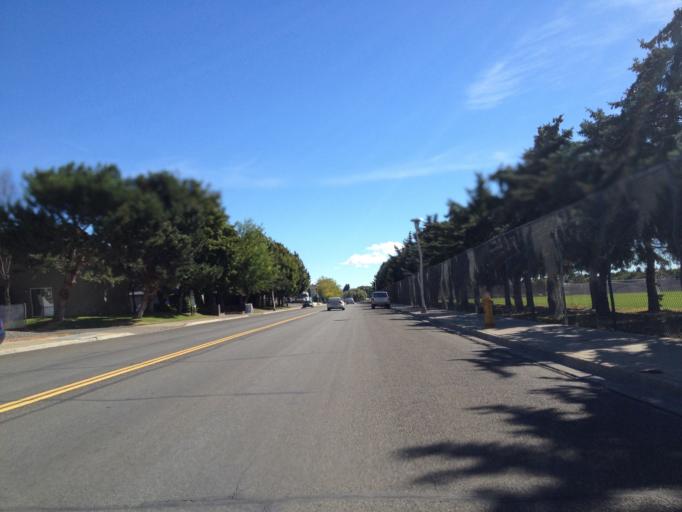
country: US
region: Washington
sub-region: Kittitas County
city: Ellensburg
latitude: 47.0103
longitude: -120.5362
